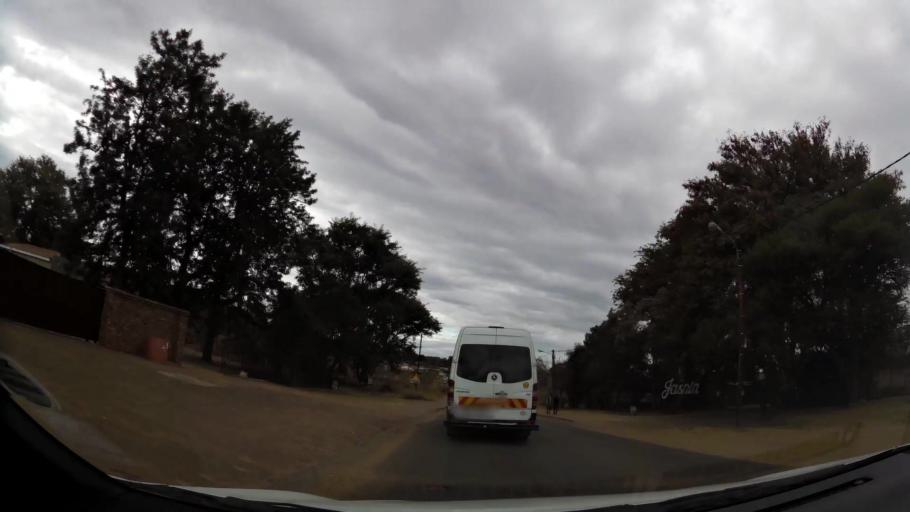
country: ZA
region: Limpopo
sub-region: Waterberg District Municipality
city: Modimolle
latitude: -24.7031
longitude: 28.4123
